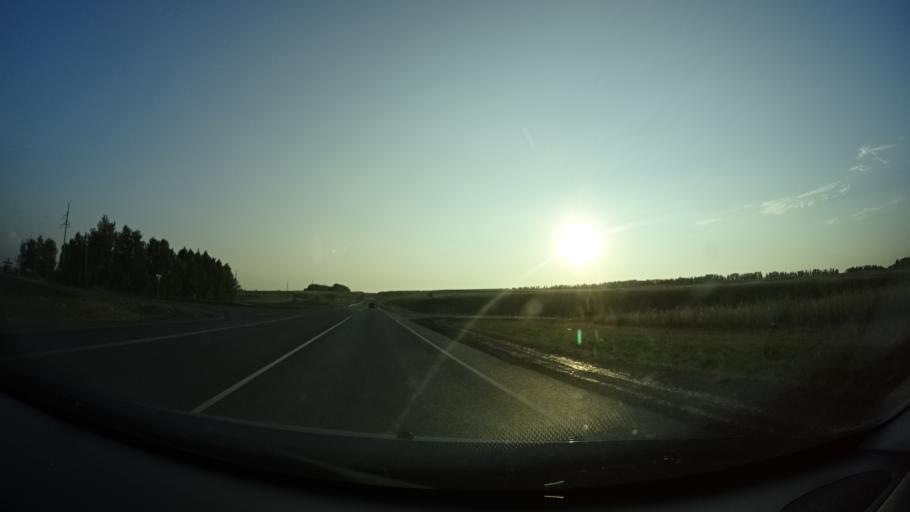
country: RU
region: Samara
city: Klyavlino
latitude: 54.0216
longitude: 51.8283
